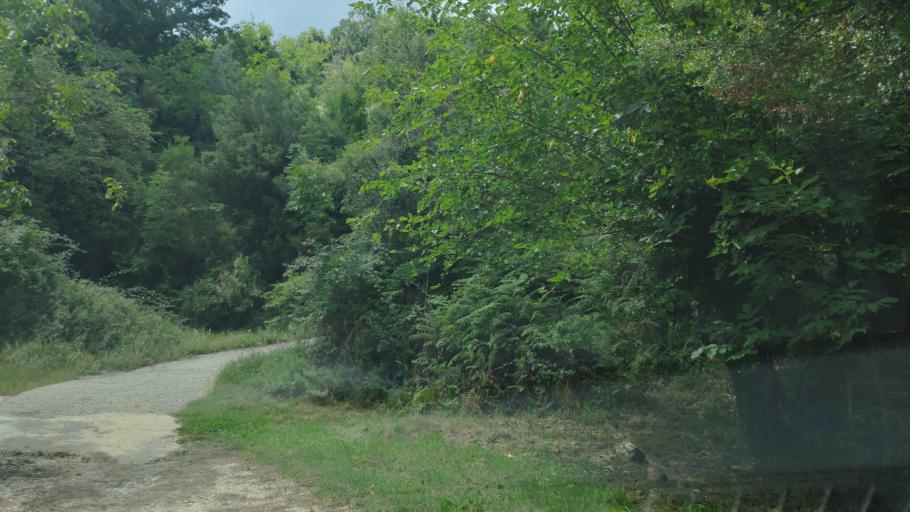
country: GR
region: Epirus
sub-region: Nomos Artas
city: Agios Dimitrios
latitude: 39.3210
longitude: 21.0061
